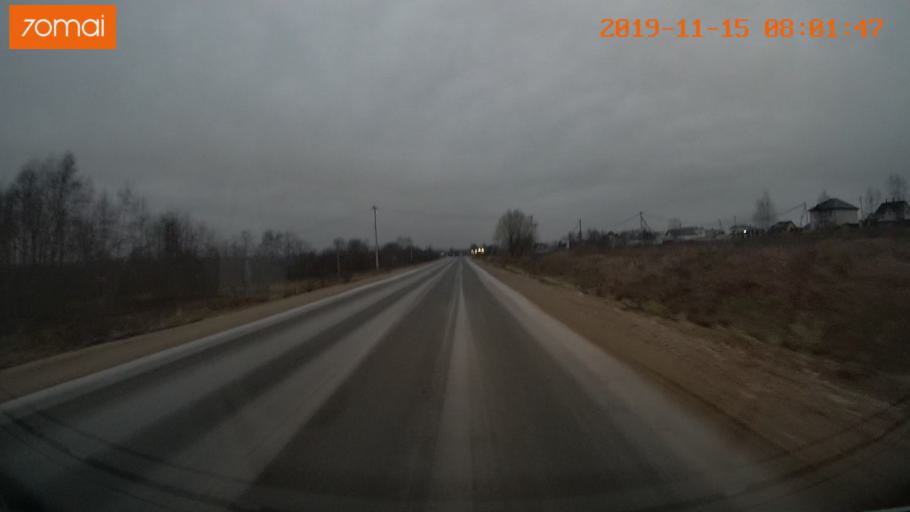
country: RU
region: Vologda
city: Cherepovets
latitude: 58.9749
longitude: 38.1138
